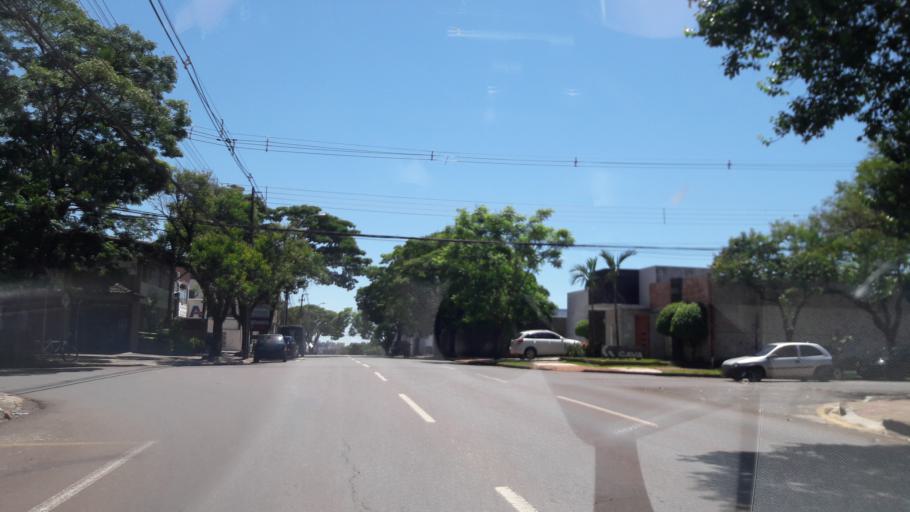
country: BR
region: Parana
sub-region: Cascavel
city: Cascavel
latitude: -24.9508
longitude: -53.4443
